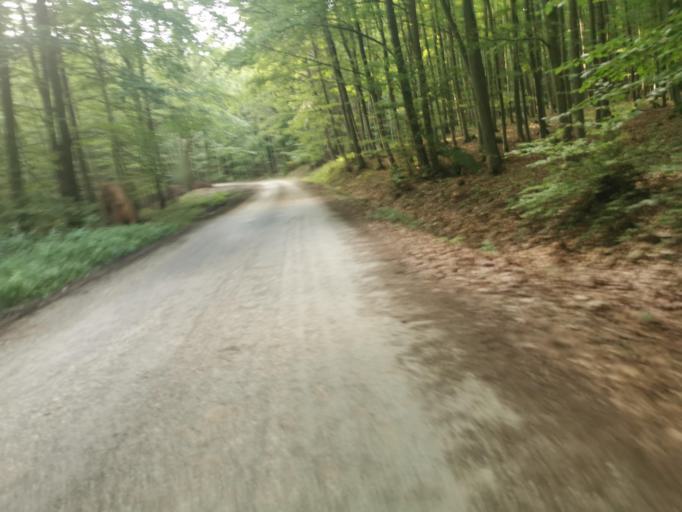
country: SK
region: Trenciansky
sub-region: Okres Myjava
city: Myjava
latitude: 48.7928
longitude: 17.6092
